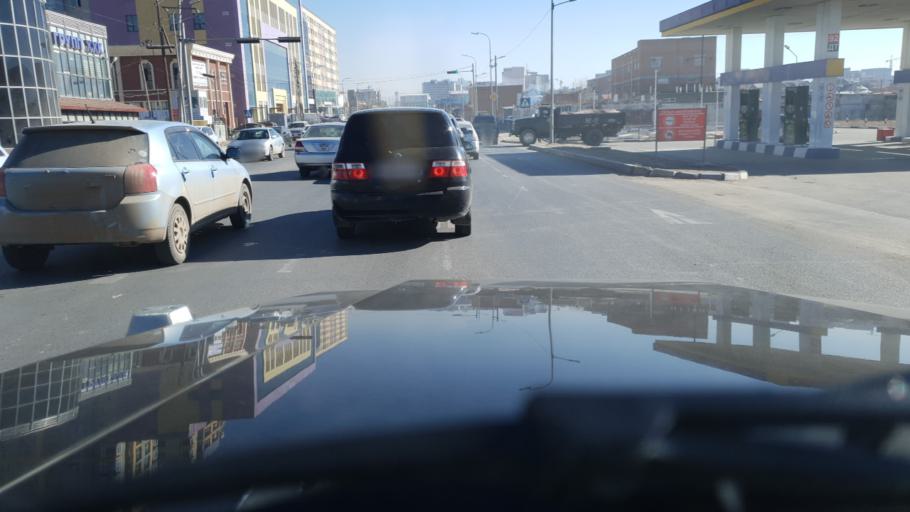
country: MN
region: Ulaanbaatar
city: Ulaanbaatar
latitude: 47.9239
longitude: 106.9650
